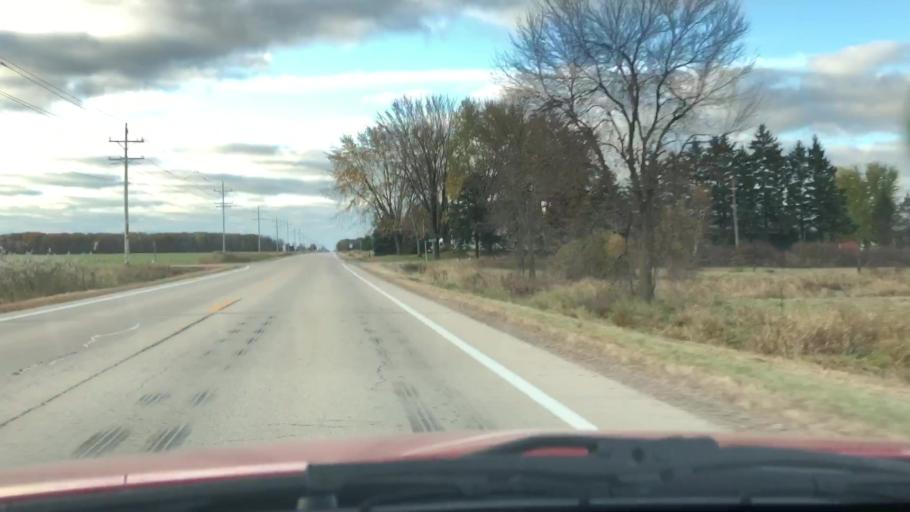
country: US
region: Wisconsin
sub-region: Outagamie County
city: Seymour
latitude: 44.4734
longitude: -88.2911
